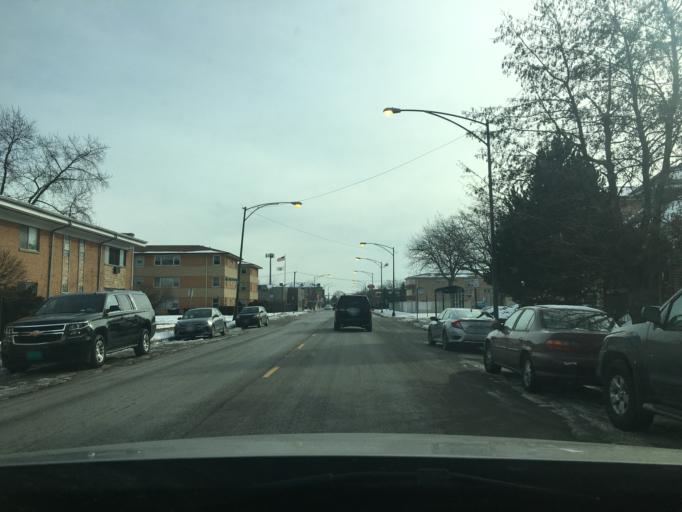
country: US
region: Illinois
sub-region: Cook County
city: Harwood Heights
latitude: 41.9773
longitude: -87.7909
